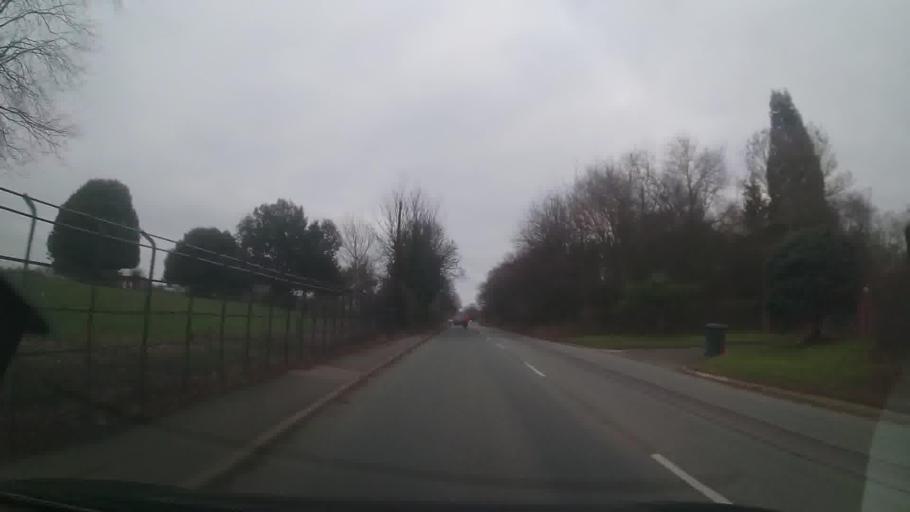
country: GB
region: England
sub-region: Shropshire
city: Bicton
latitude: 52.7213
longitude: -2.8015
